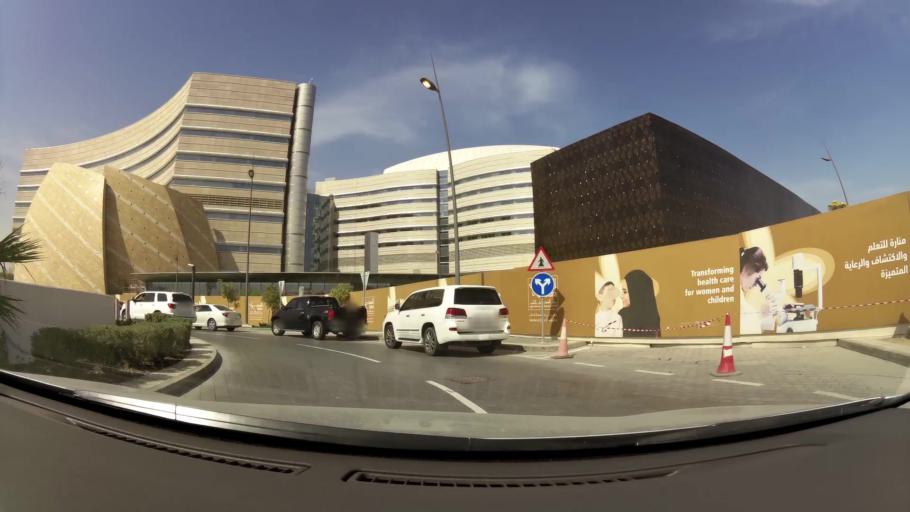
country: QA
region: Baladiyat ar Rayyan
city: Ar Rayyan
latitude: 25.3208
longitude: 51.4435
